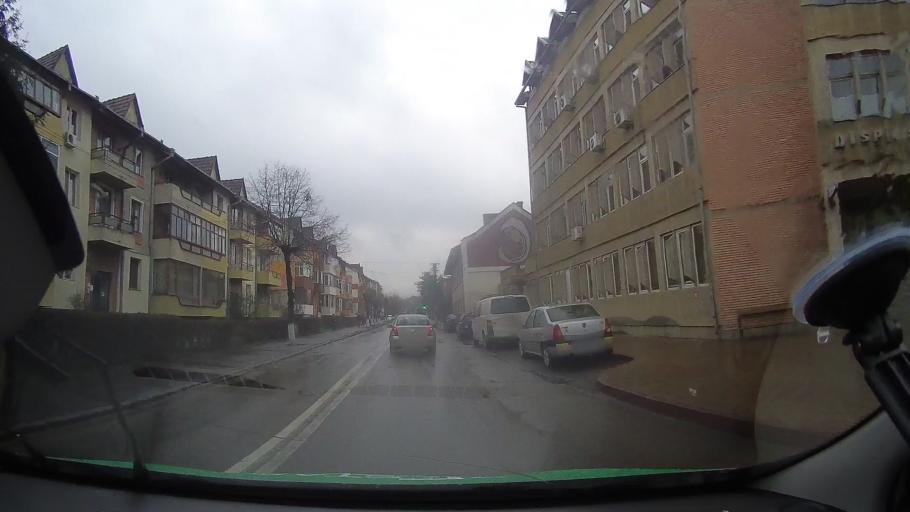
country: RO
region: Hunedoara
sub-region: Municipiul Brad
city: Brad
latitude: 46.1265
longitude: 22.7916
